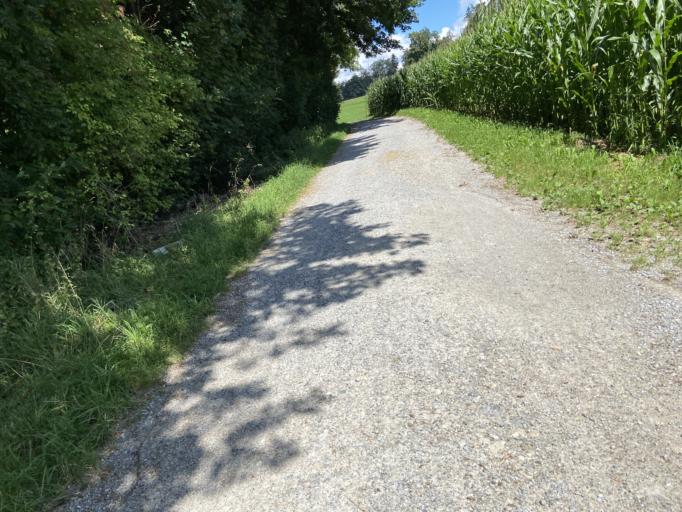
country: CH
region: Zurich
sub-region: Bezirk Meilen
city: Oetwil am See
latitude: 47.2574
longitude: 8.7163
